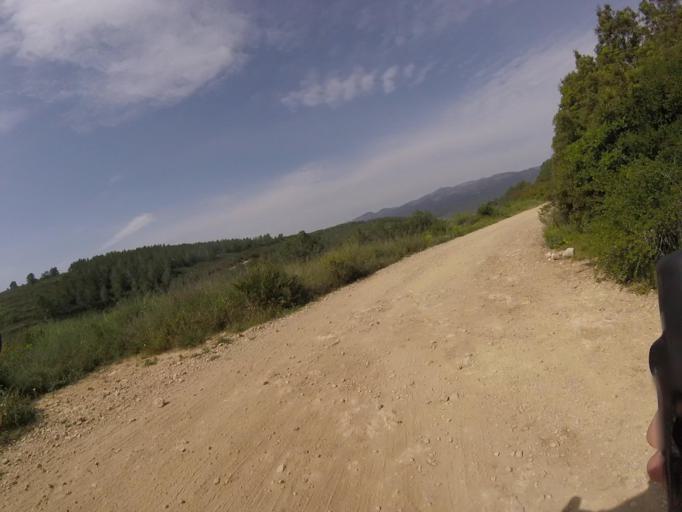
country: ES
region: Valencia
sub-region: Provincia de Castello
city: Cuevas de Vinroma
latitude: 40.2921
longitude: 0.1272
